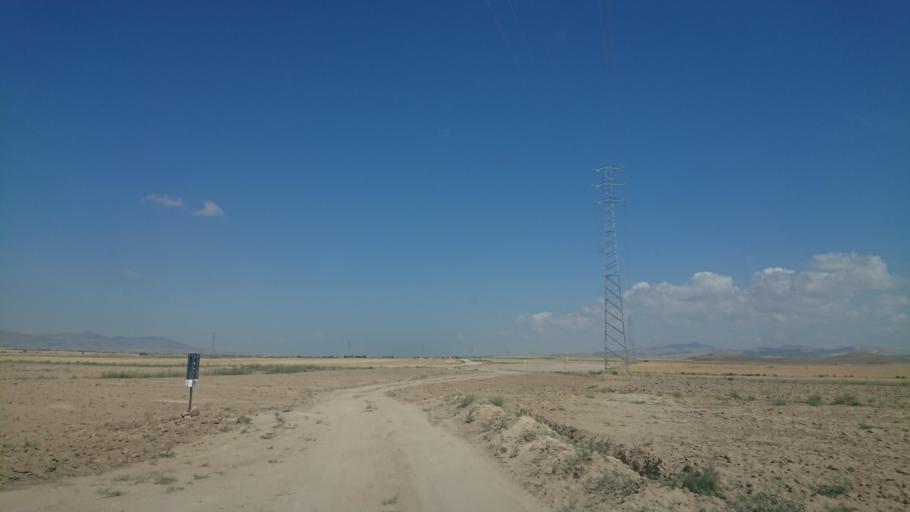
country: TR
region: Aksaray
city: Sariyahsi
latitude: 39.0009
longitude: 33.8902
